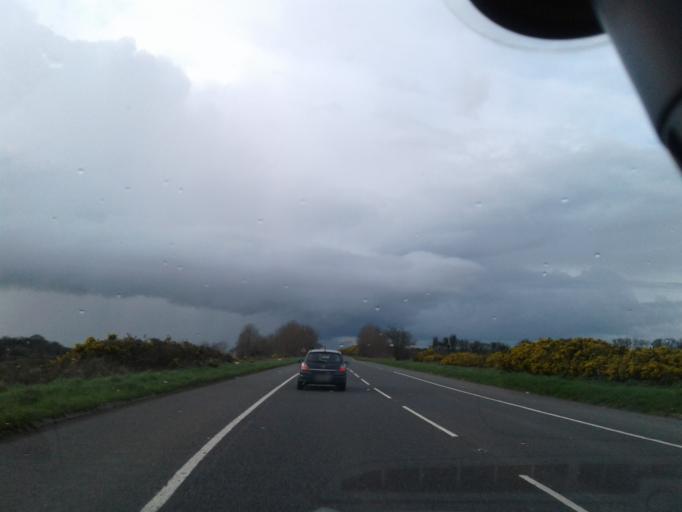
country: GB
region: Northern Ireland
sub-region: Strabane District
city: Sion Mills
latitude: 54.7398
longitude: -7.4371
